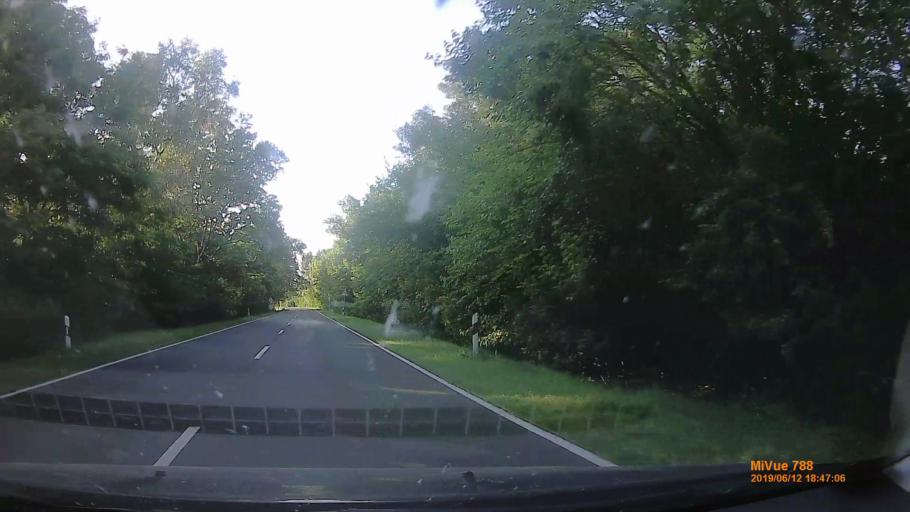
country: HU
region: Bacs-Kiskun
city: Palmonostora
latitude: 46.6034
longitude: 19.9190
